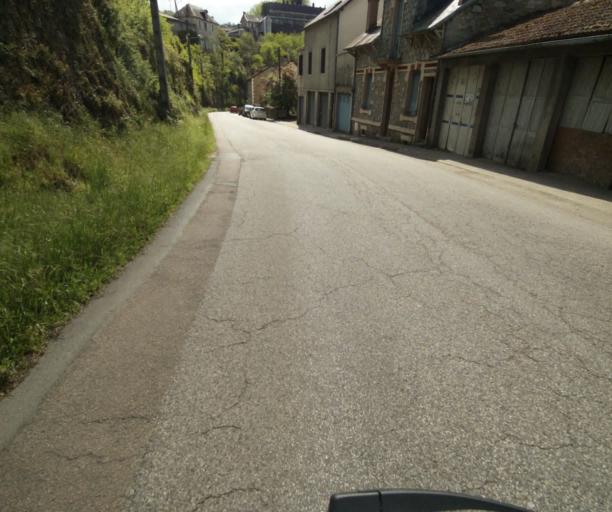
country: FR
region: Limousin
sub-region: Departement de la Correze
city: Tulle
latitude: 45.2745
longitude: 1.7714
